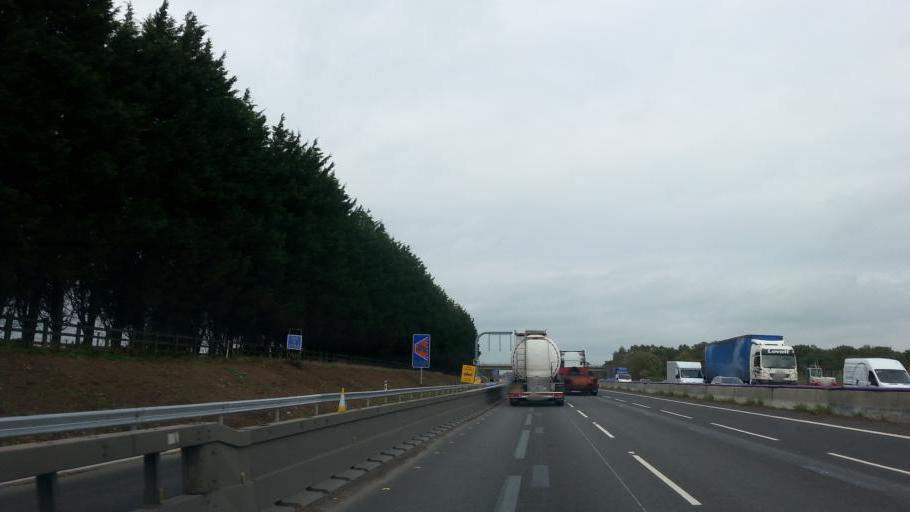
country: GB
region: England
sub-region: Cheshire East
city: Holmes Chapel
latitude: 53.2143
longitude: -2.3889
